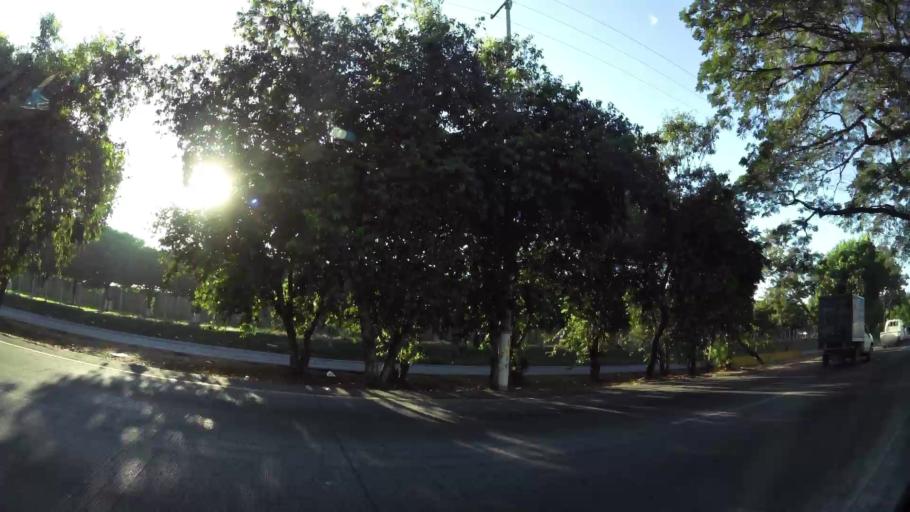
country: SV
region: La Libertad
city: Santa Tecla
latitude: 13.7476
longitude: -89.3643
